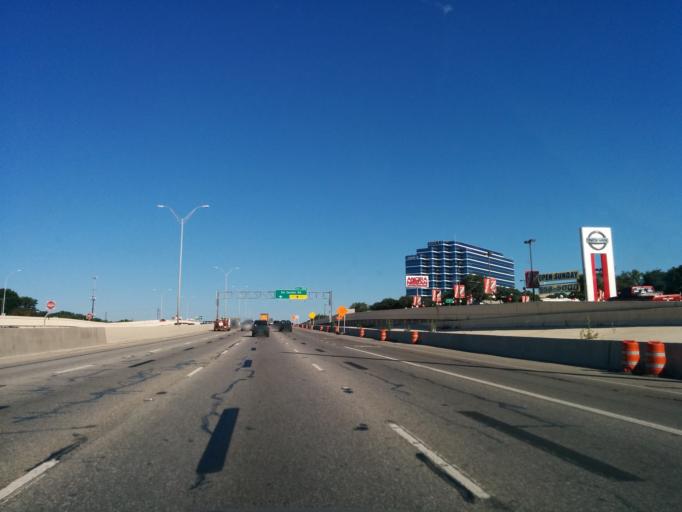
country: US
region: Texas
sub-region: Bexar County
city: Shavano Park
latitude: 29.5424
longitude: -98.5752
